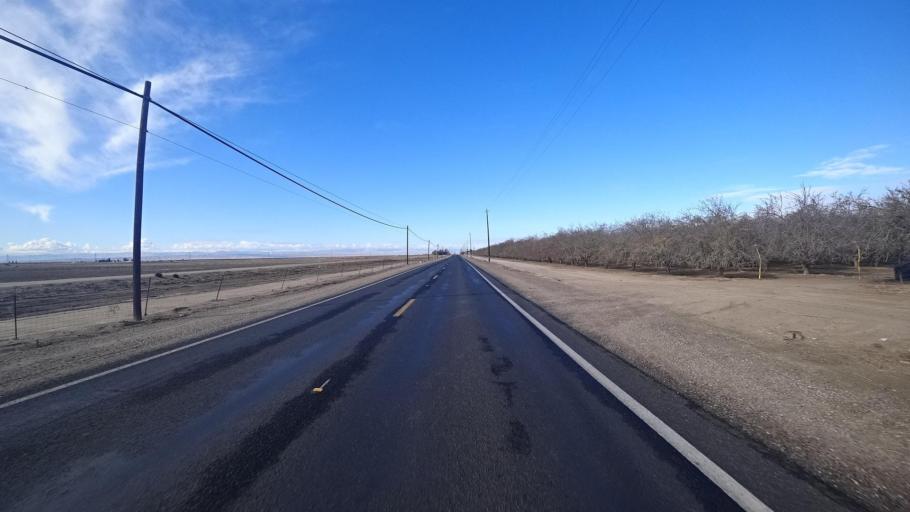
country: US
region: California
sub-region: Kern County
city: Rosedale
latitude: 35.3834
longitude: -119.2384
